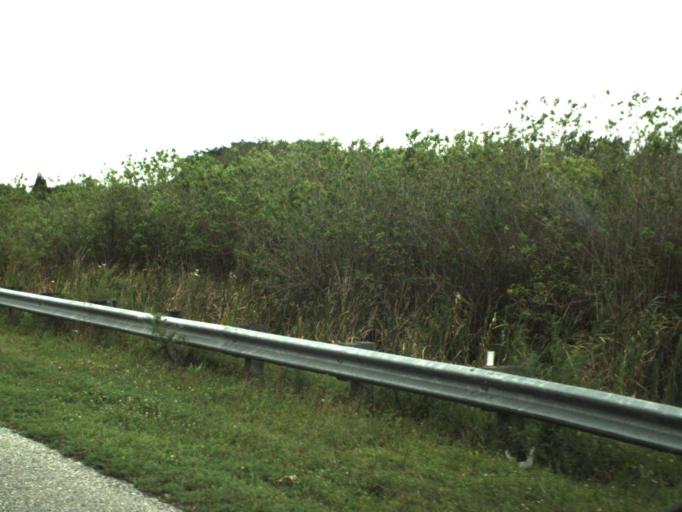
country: US
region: Florida
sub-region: Brevard County
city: Titusville
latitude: 28.5507
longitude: -80.8854
